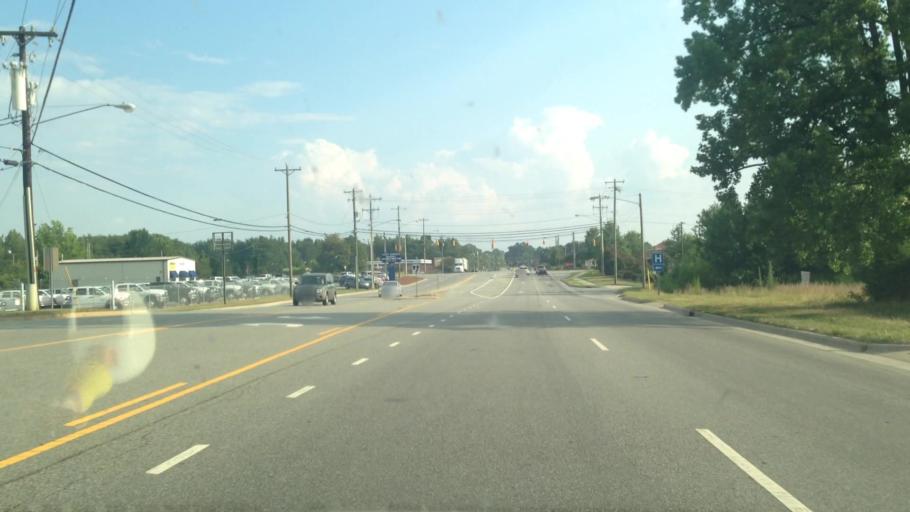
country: US
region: North Carolina
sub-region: Forsyth County
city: Kernersville
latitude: 36.0925
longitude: -80.0616
